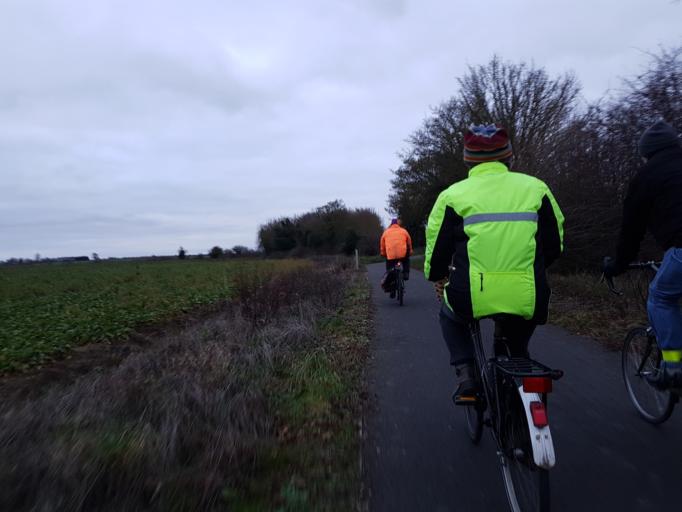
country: GB
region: England
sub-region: Cambridgeshire
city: Bottisham
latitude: 52.2312
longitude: 0.2357
